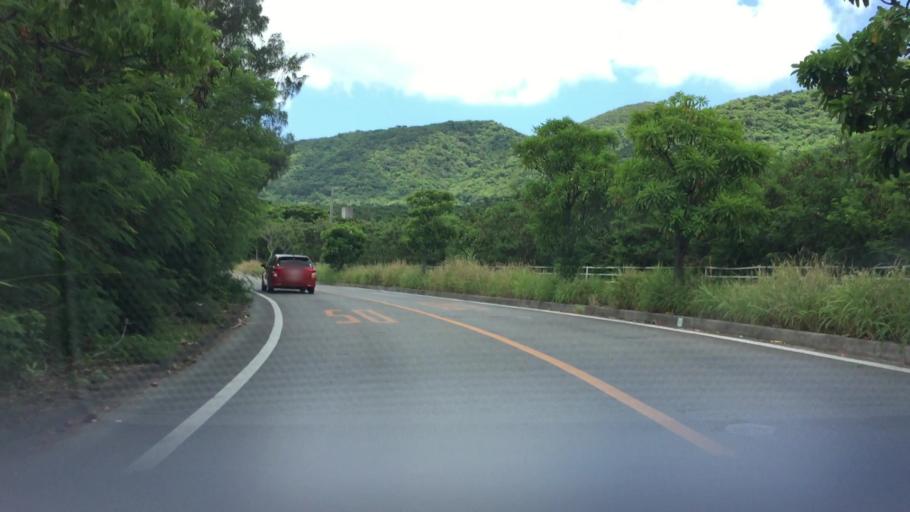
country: JP
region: Okinawa
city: Ishigaki
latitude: 24.4183
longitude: 124.1345
